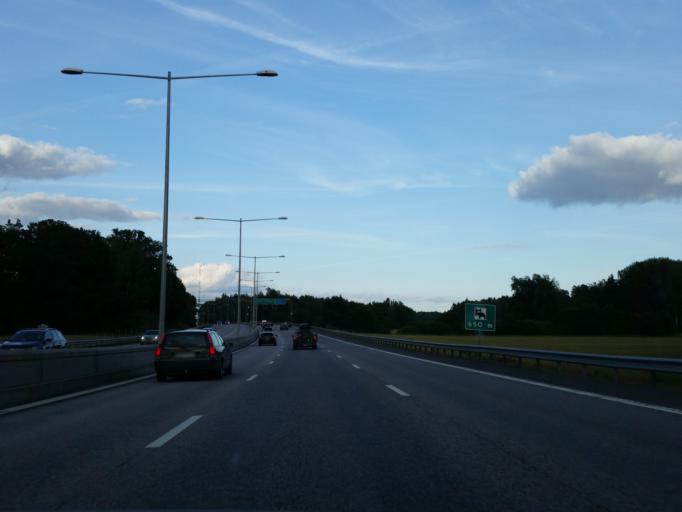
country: SE
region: Stockholm
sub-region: Salems Kommun
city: Ronninge
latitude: 59.2108
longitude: 17.7318
